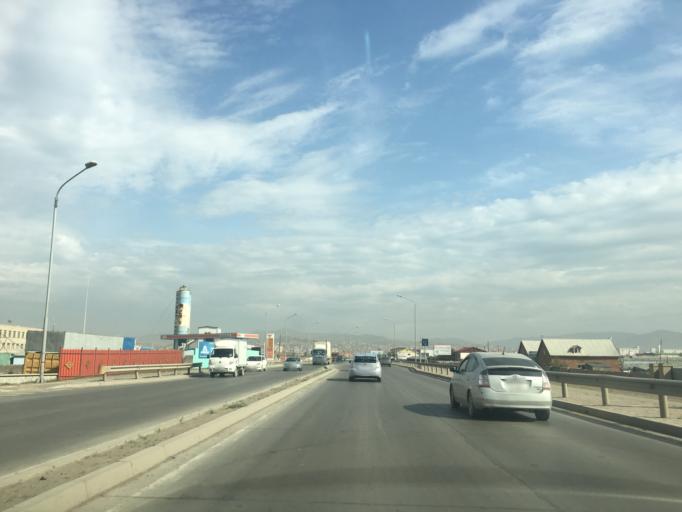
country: MN
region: Ulaanbaatar
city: Ulaanbaatar
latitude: 47.8931
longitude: 106.7854
